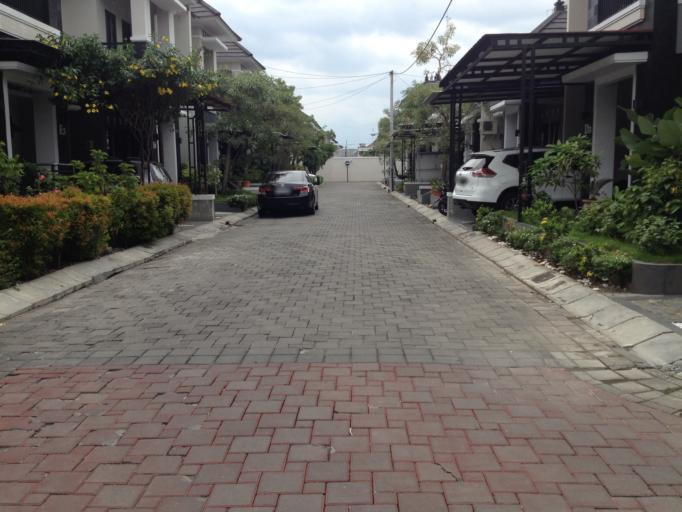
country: ID
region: Daerah Istimewa Yogyakarta
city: Yogyakarta
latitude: -7.8201
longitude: 110.3846
